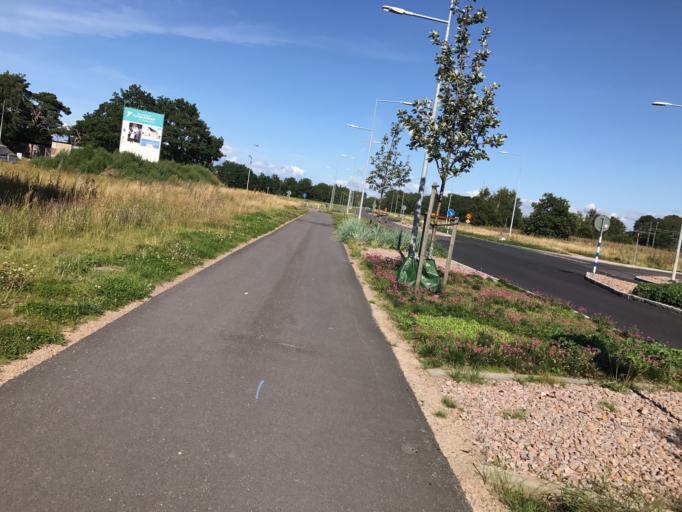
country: SE
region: Skane
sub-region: Bastads Kommun
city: Bastad
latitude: 56.4330
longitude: 12.9070
